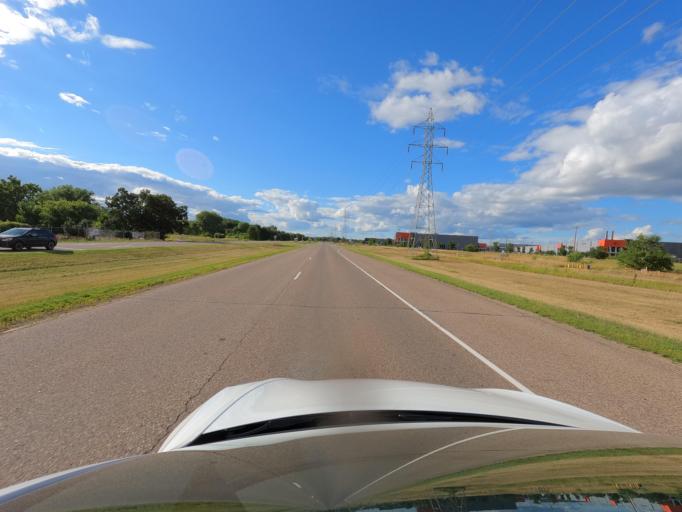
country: US
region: Minnesota
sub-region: Anoka County
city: Columbia Heights
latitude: 45.0505
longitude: -93.2763
